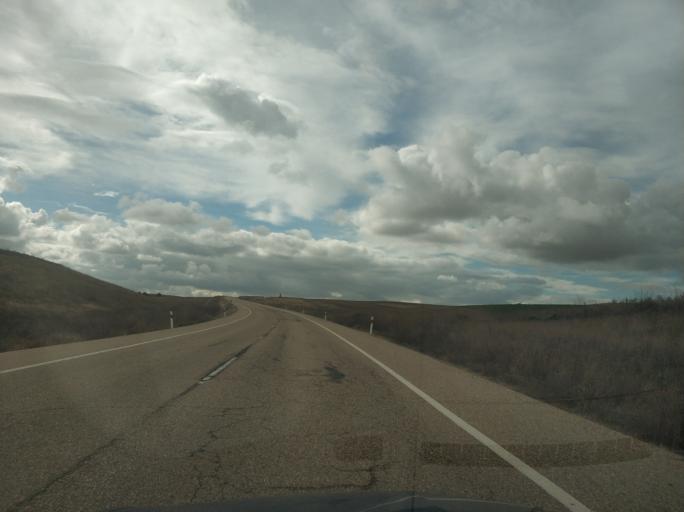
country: ES
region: Castille and Leon
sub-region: Provincia de Valladolid
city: Pollos
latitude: 41.4412
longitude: -5.0943
